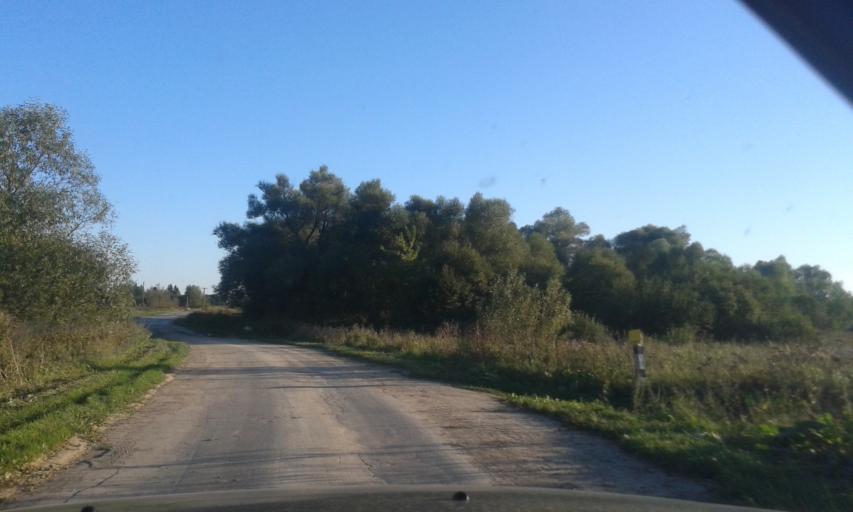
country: RU
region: Tula
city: Krapivna
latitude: 54.1216
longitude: 37.1531
